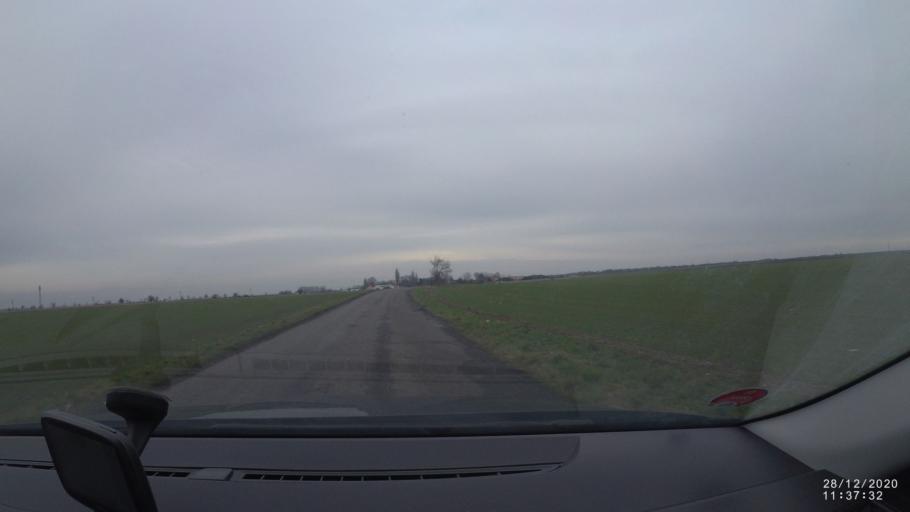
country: CZ
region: Praha
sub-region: Praha 20
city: Horni Pocernice
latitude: 50.1409
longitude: 14.6217
